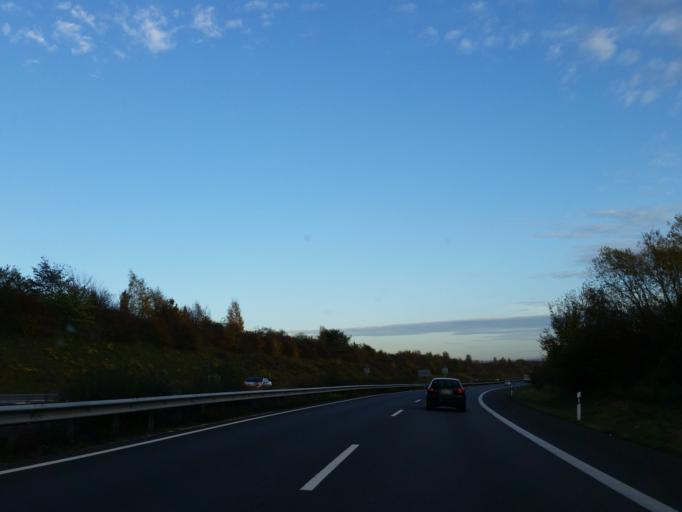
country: DE
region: Lower Saxony
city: Braunschweig
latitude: 52.2514
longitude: 10.5750
